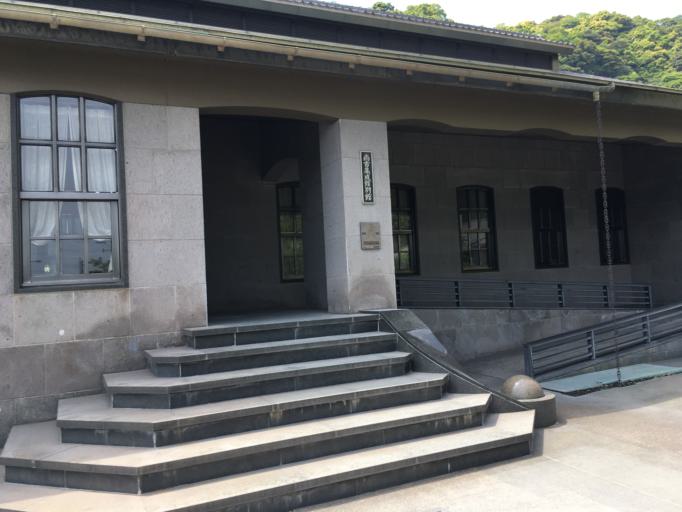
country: JP
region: Kagoshima
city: Kagoshima-shi
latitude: 31.6169
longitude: 130.5763
